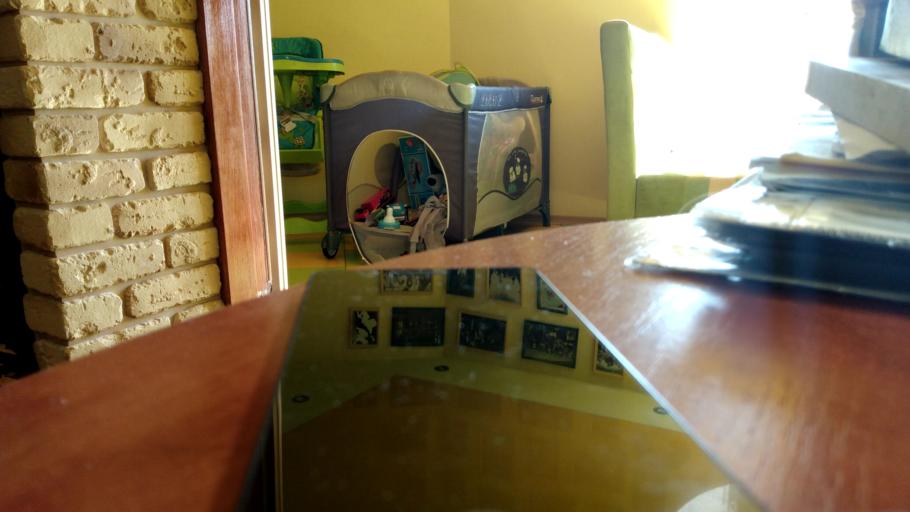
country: RU
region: Penza
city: Serdobsk
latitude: 52.3042
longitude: 44.3952
